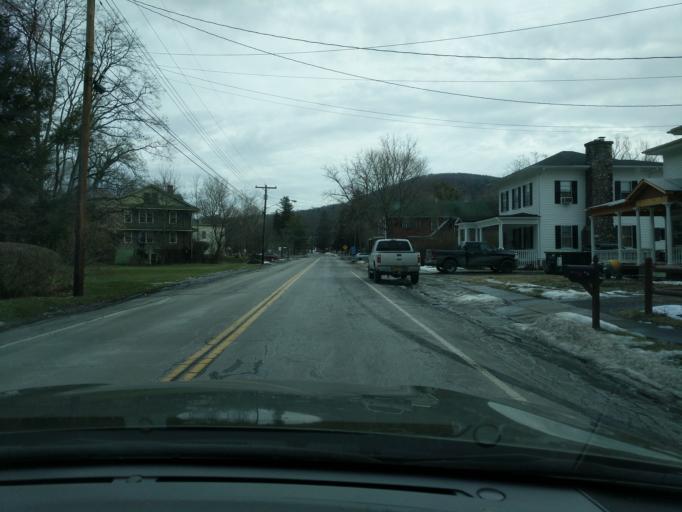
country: US
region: New York
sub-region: Tompkins County
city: East Ithaca
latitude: 42.3819
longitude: -76.3980
